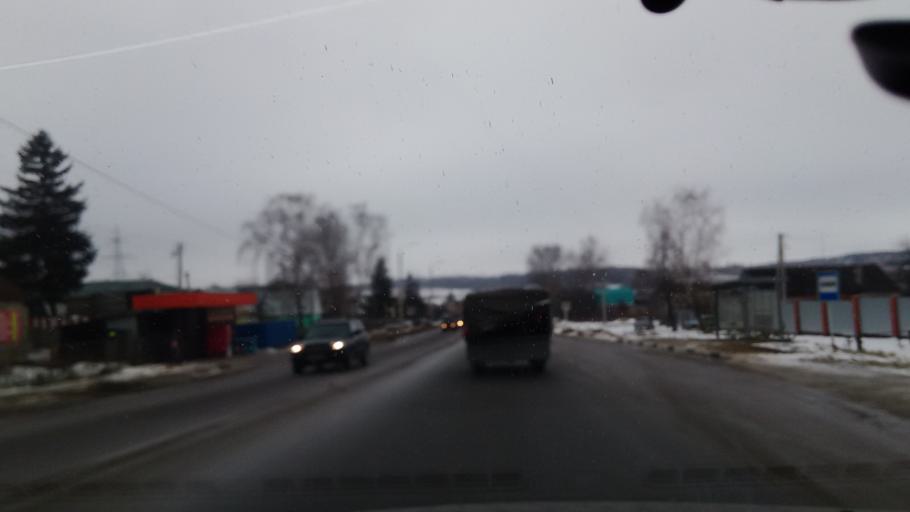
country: RU
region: Tula
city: Skuratovskiy
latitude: 54.1372
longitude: 37.6761
